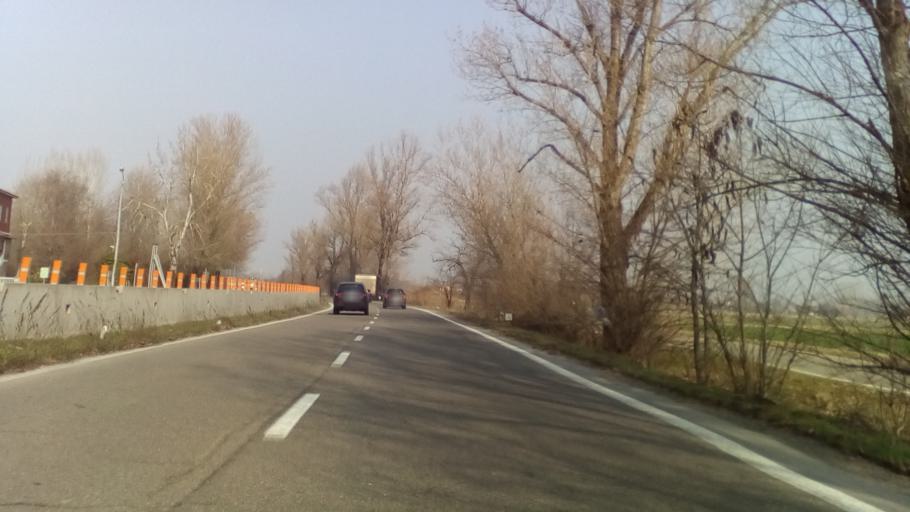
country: IT
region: Emilia-Romagna
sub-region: Provincia di Modena
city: Modena
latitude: 44.6169
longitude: 10.9405
